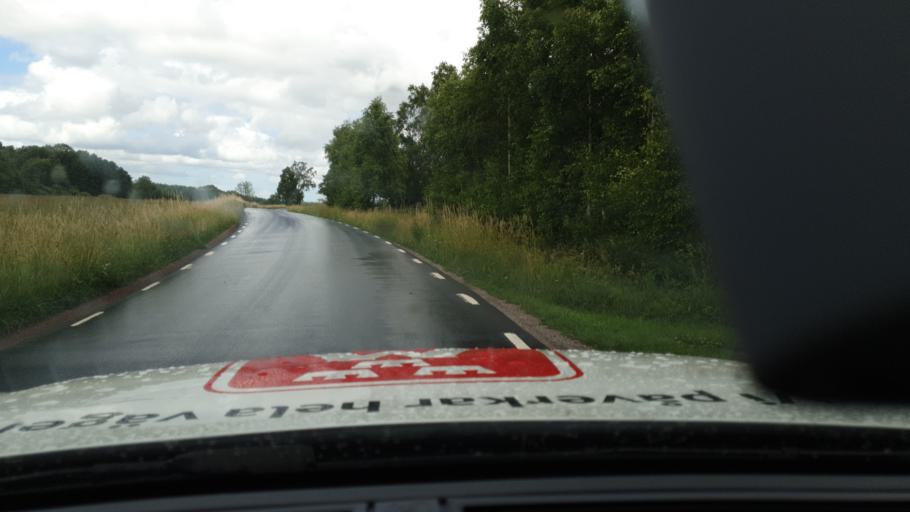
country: SE
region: Vaestra Goetaland
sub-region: Falkopings Kommun
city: Akarp
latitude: 58.2713
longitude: 13.6033
